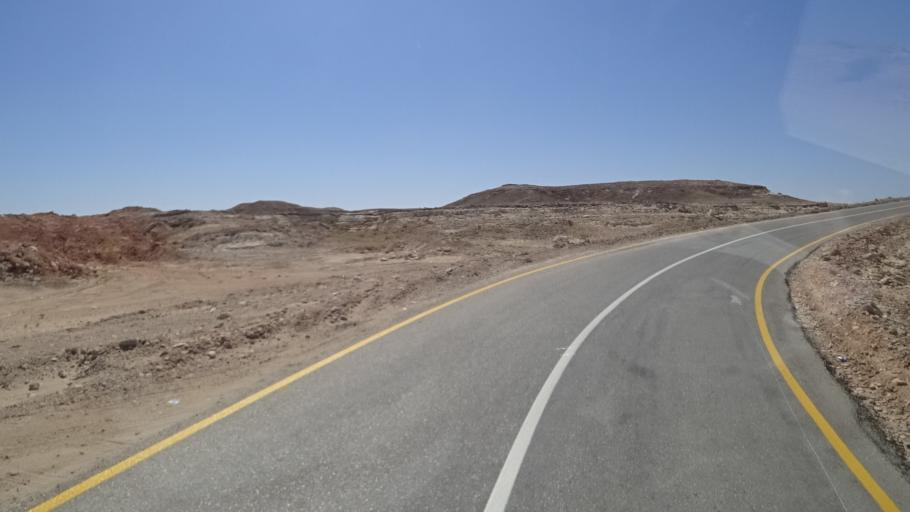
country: OM
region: Zufar
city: Salalah
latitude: 17.4761
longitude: 53.3522
